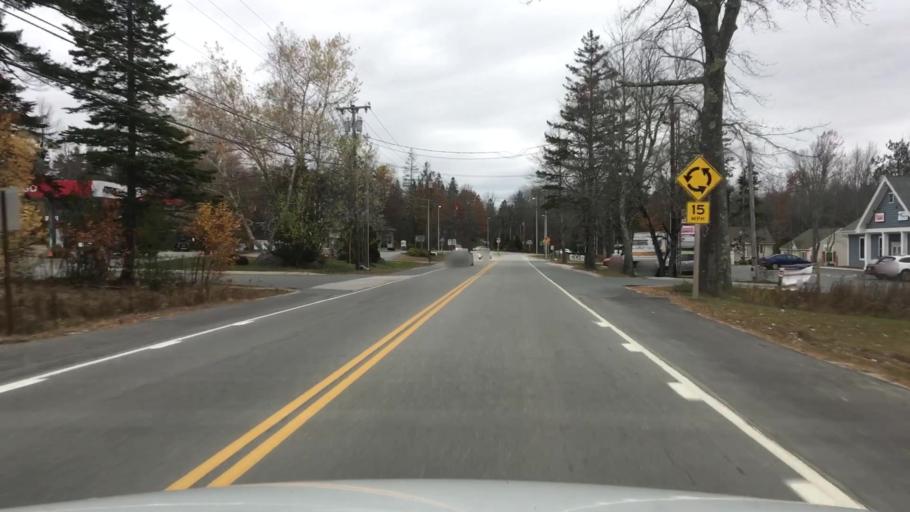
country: US
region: Maine
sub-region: Hancock County
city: Sedgwick
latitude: 44.4067
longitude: -68.5959
